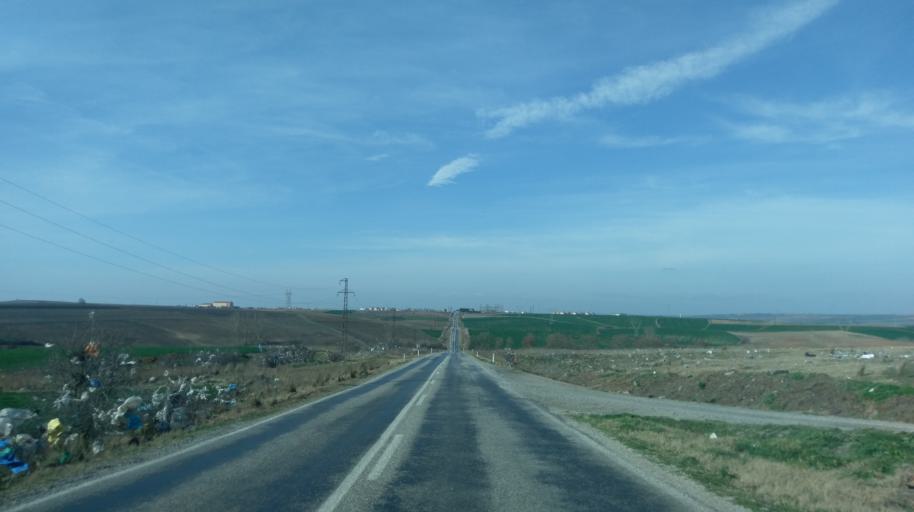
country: TR
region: Edirne
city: Uzun Keupru
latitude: 41.2735
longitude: 26.7329
